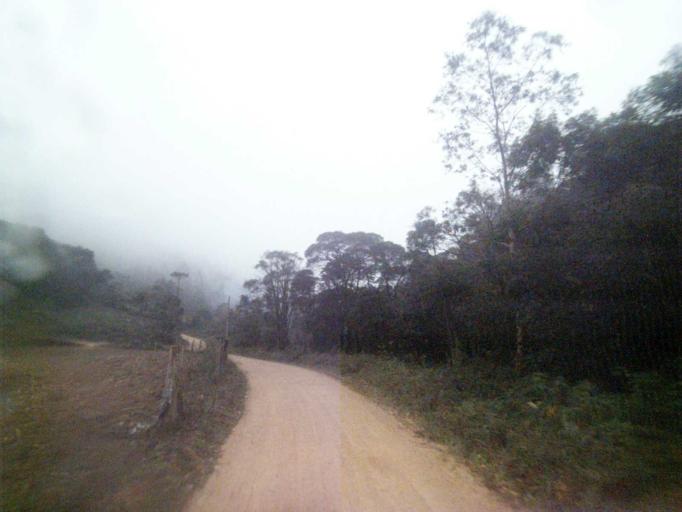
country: BR
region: Santa Catarina
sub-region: Anitapolis
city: Anitapolis
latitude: -27.8112
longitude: -49.1405
